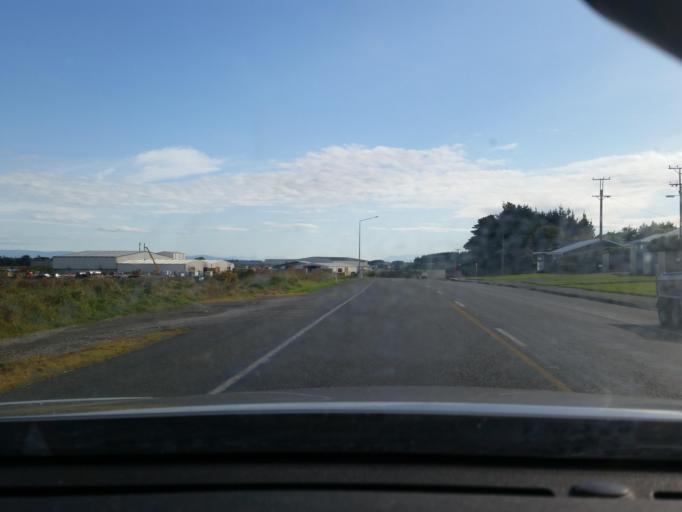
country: NZ
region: Southland
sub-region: Invercargill City
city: Invercargill
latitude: -46.4551
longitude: 168.3644
